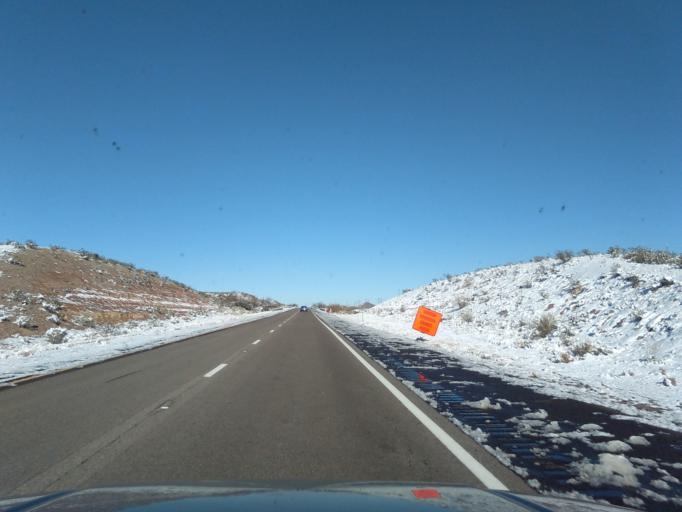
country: US
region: New Mexico
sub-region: Socorro County
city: Socorro
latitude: 33.7004
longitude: -107.0498
